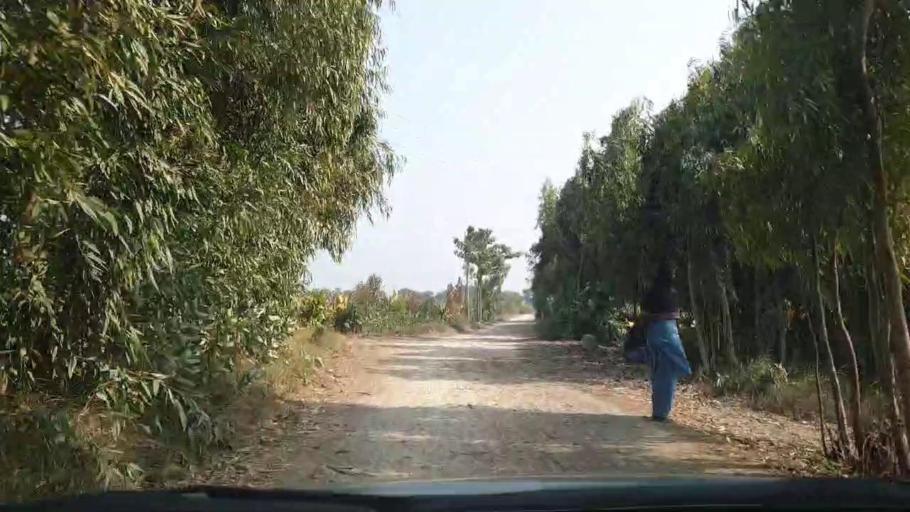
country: PK
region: Sindh
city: Matiari
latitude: 25.6470
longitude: 68.5568
